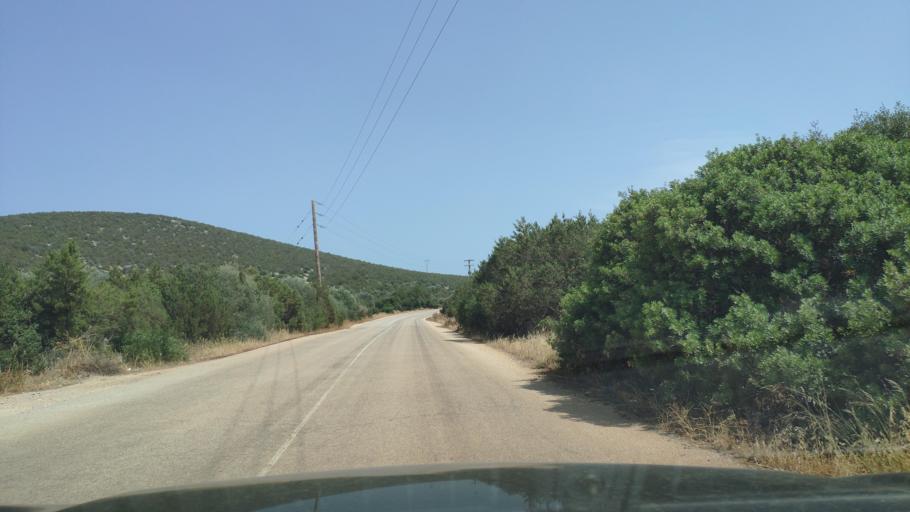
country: GR
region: Peloponnese
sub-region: Nomos Argolidos
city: Didyma
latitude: 37.4501
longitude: 23.1783
